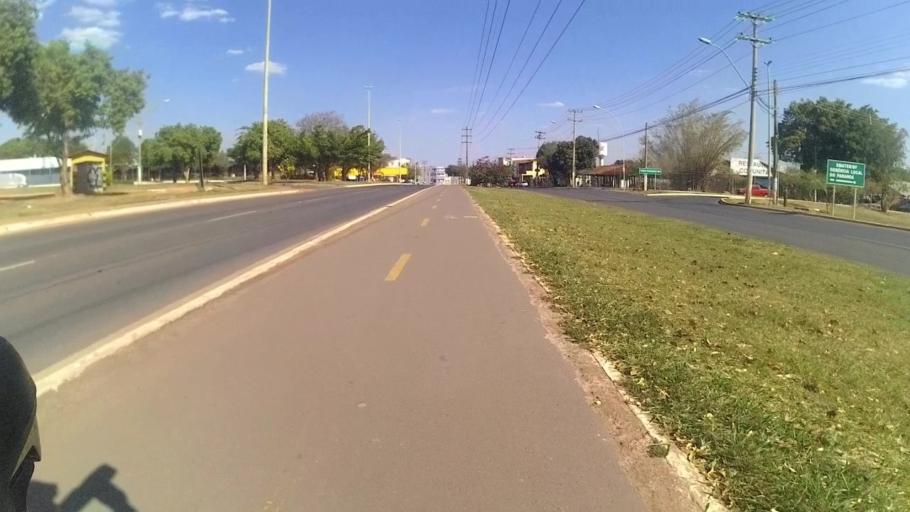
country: BR
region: Federal District
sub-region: Brasilia
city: Brasilia
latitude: -15.7788
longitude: -47.7811
